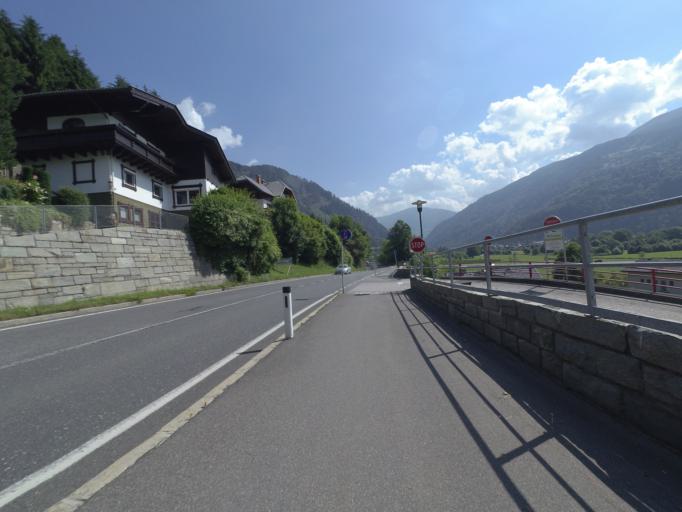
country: AT
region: Carinthia
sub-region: Politischer Bezirk Villach Land
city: Ferndorf
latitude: 46.7772
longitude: 13.6412
